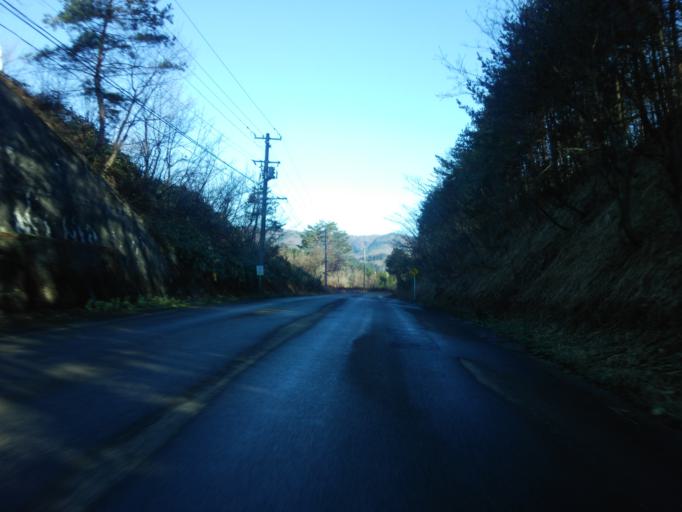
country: JP
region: Fukushima
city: Kitakata
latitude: 37.6993
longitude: 139.7881
